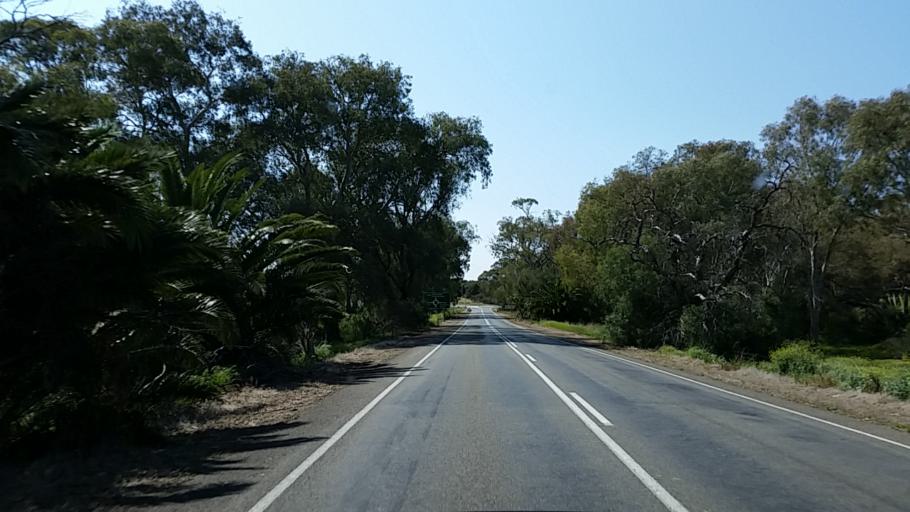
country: AU
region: South Australia
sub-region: Port Pirie City and Dists
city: Crystal Brook
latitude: -33.2646
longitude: 138.3416
